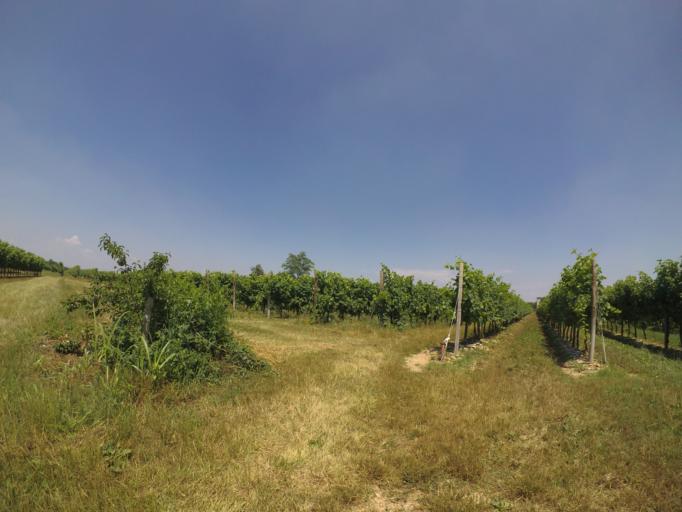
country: IT
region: Friuli Venezia Giulia
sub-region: Provincia di Udine
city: Bertiolo
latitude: 45.9479
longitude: 13.0335
